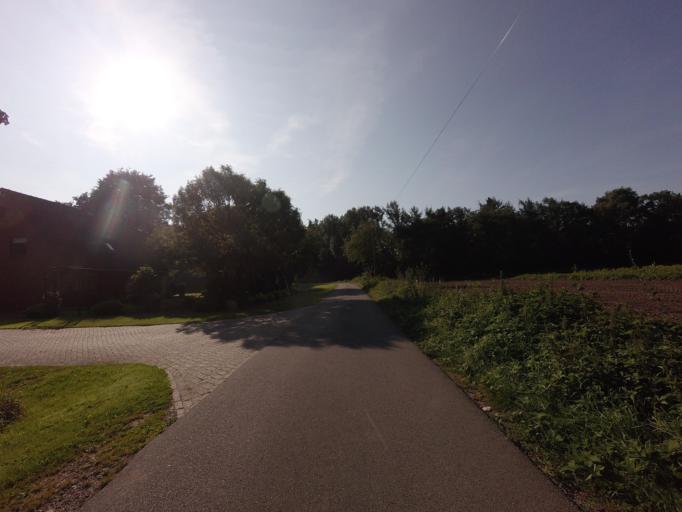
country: DE
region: Lower Saxony
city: Wielen
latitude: 52.5564
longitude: 6.7577
